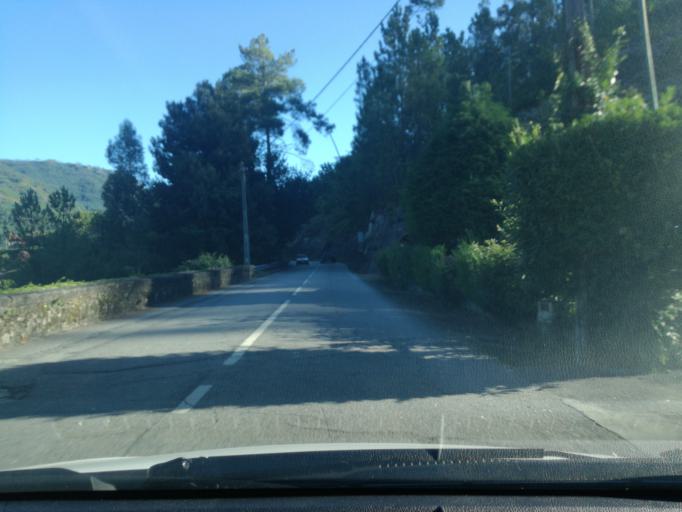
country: PT
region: Braga
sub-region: Vieira do Minho
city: Real
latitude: 41.6993
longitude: -8.1676
